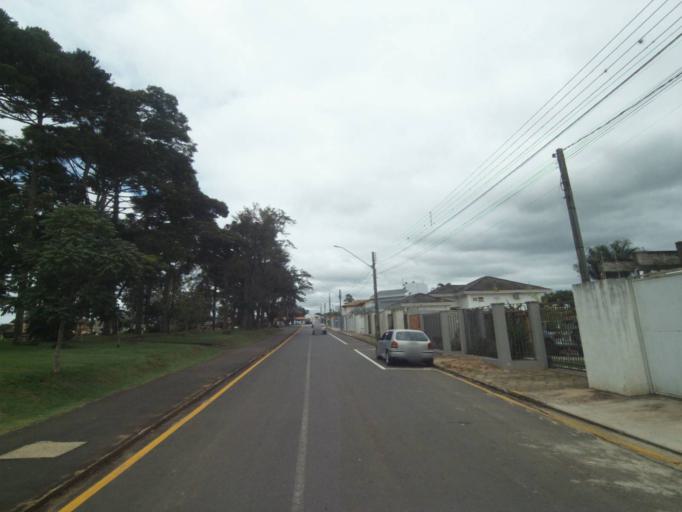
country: BR
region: Parana
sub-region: Telemaco Borba
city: Telemaco Borba
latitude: -24.3318
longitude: -50.6095
